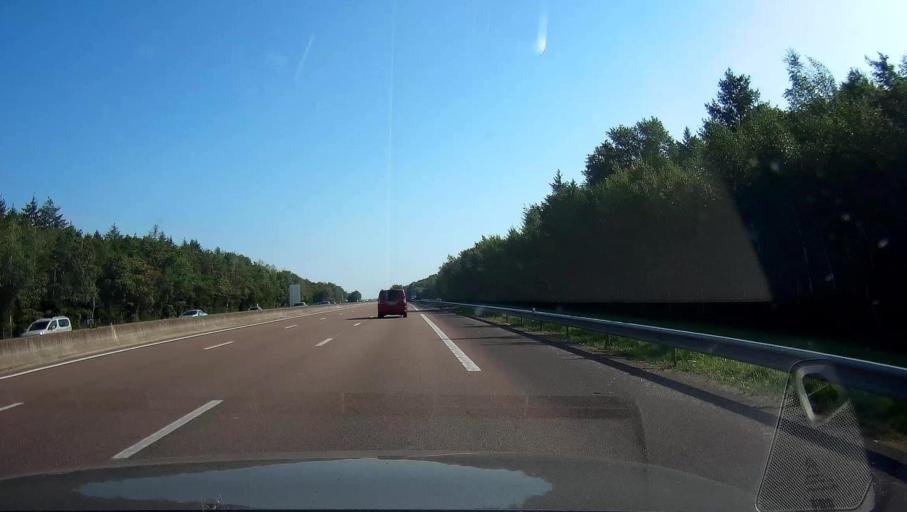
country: FR
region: Bourgogne
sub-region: Departement de la Cote-d'Or
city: Nuits-Saint-Georges
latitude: 47.0655
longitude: 4.9167
